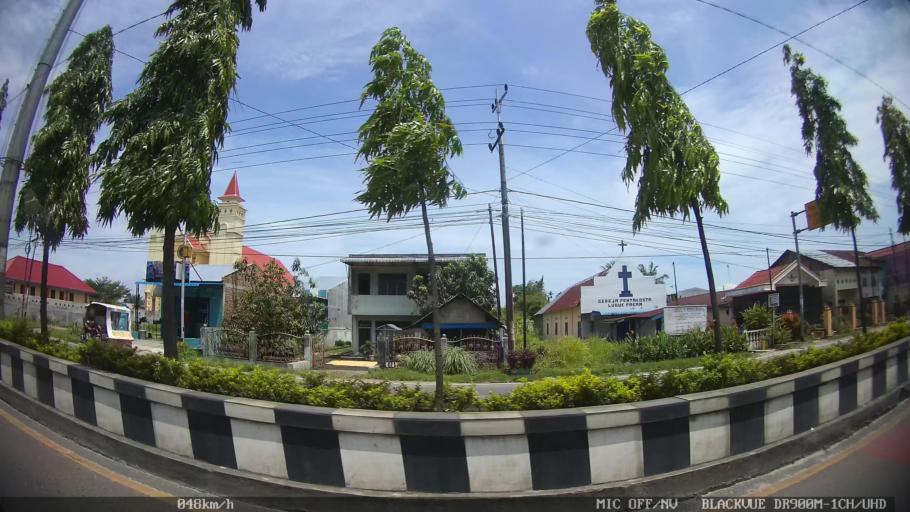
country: ID
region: North Sumatra
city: Percut
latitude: 3.5558
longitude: 98.8837
